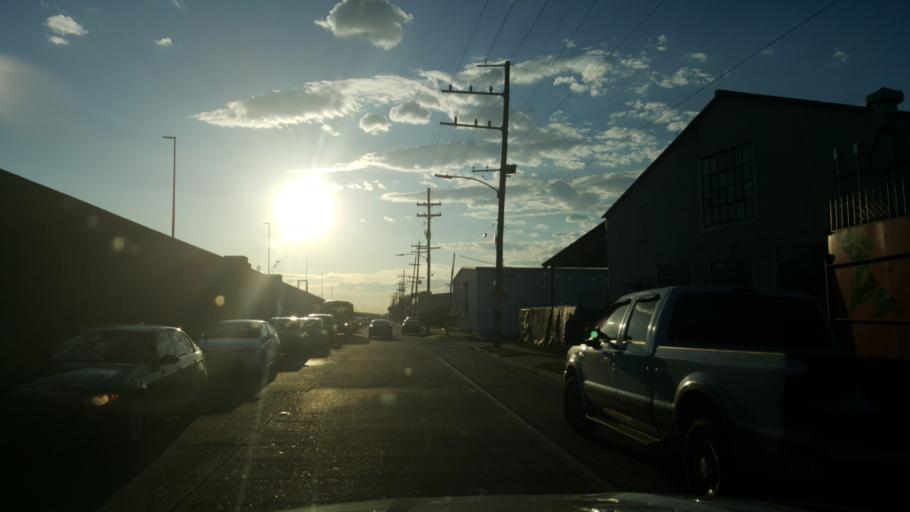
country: US
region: Louisiana
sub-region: Jefferson Parish
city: Harvey
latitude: 29.9220
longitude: -90.0742
